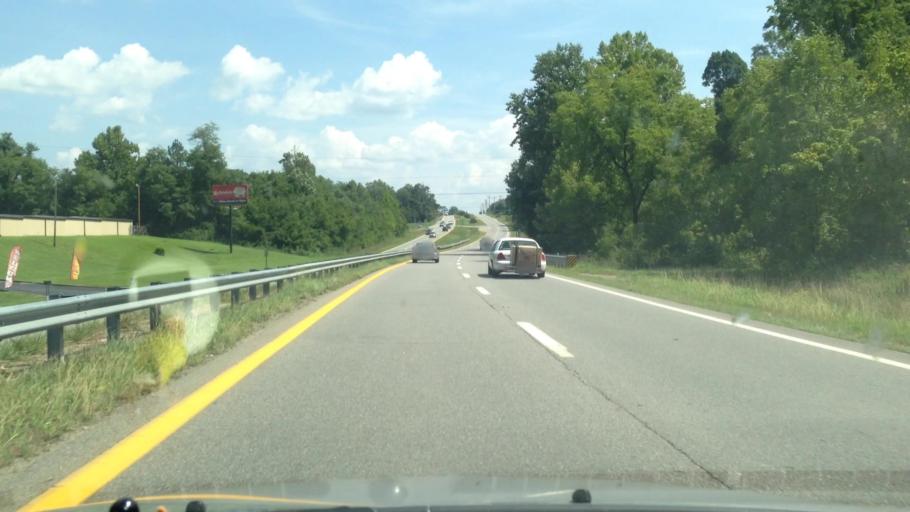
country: US
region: Virginia
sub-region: City of Martinsville
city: Martinsville
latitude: 36.6473
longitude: -79.8666
